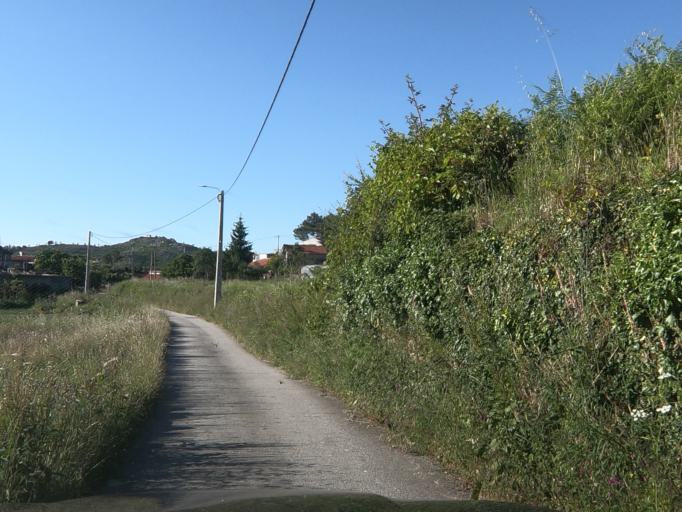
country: PT
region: Vila Real
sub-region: Vila Real
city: Vila Real
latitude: 41.3244
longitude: -7.6748
